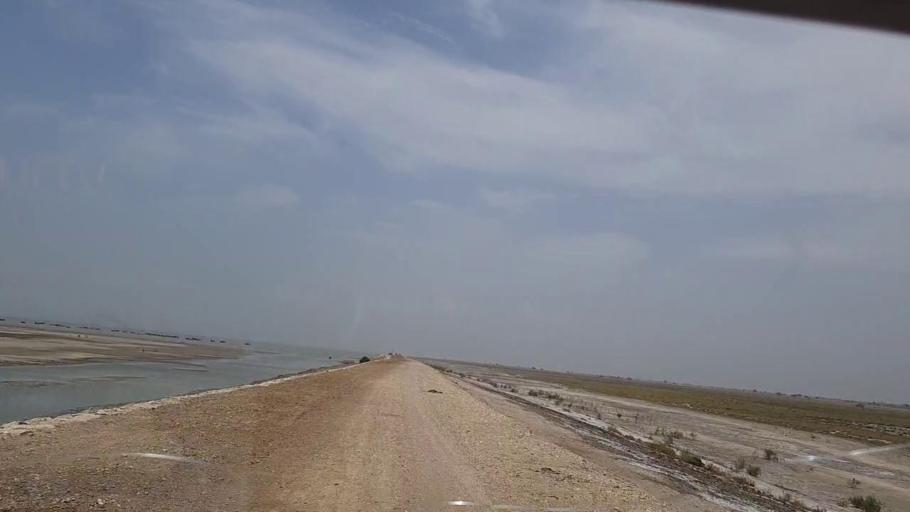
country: PK
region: Sindh
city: Sehwan
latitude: 26.4167
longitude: 67.7501
